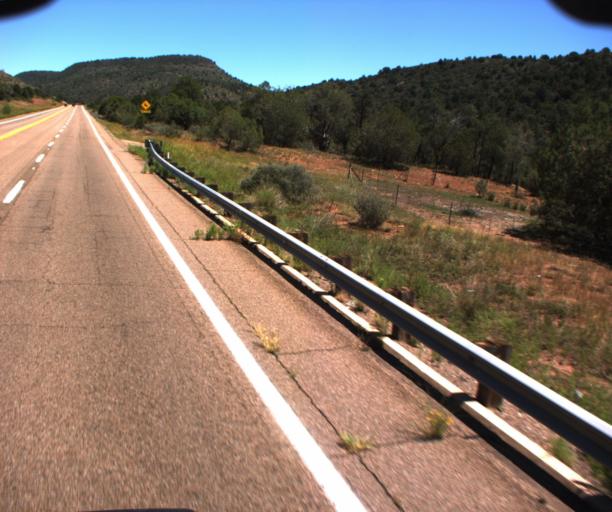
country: US
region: Arizona
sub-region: Navajo County
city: Cibecue
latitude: 33.8673
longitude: -110.4093
